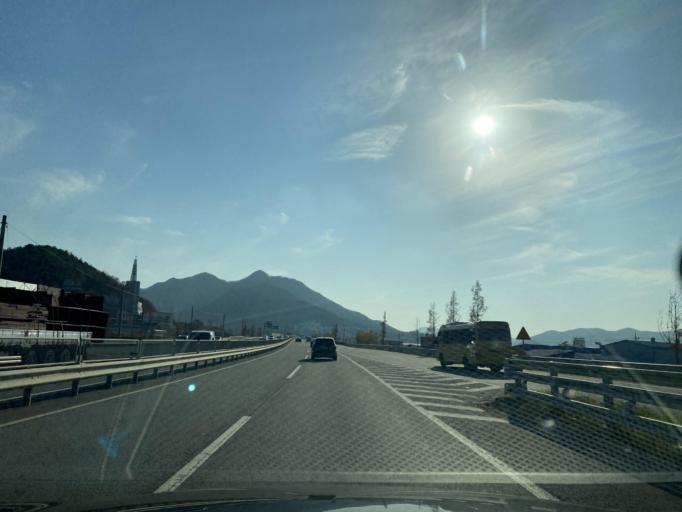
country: KR
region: Chungcheongnam-do
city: Asan
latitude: 36.7676
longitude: 127.0383
